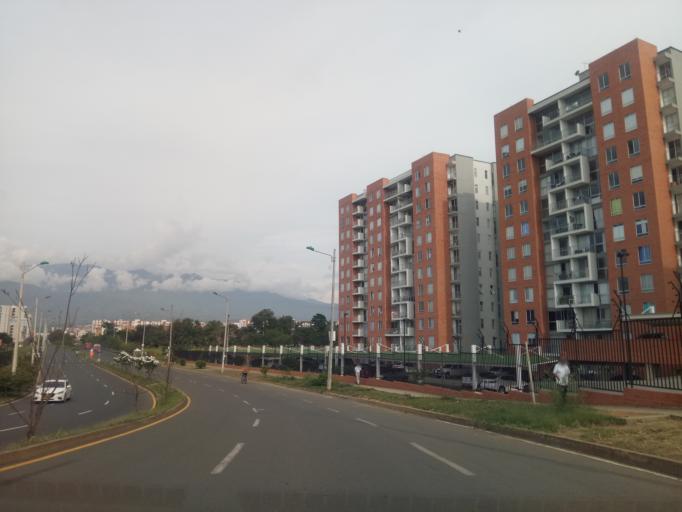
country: CO
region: Valle del Cauca
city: Cali
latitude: 3.3682
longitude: -76.5105
